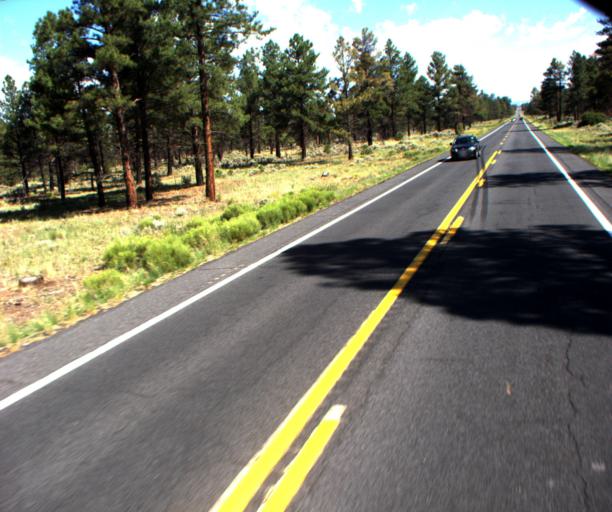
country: US
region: Arizona
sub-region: Coconino County
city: Grand Canyon Village
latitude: 35.9109
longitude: -112.1297
